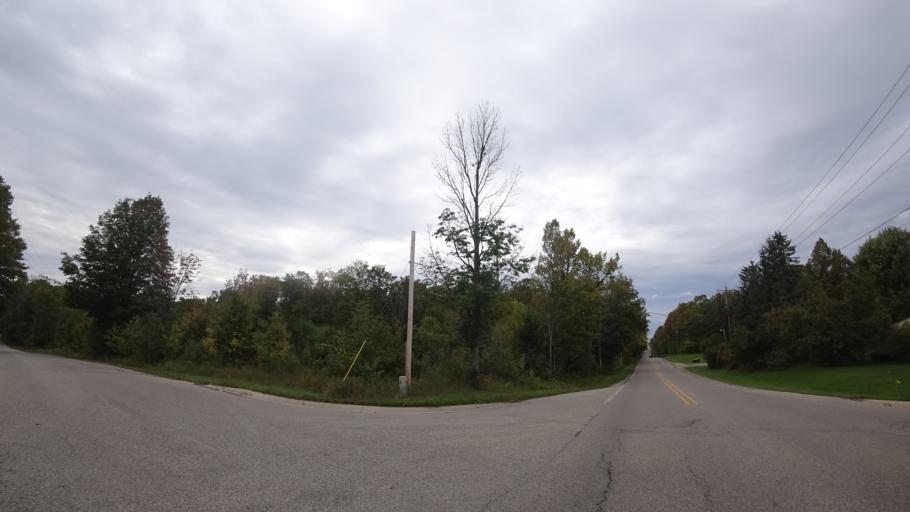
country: US
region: Michigan
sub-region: Emmet County
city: Petoskey
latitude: 45.3411
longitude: -84.9755
